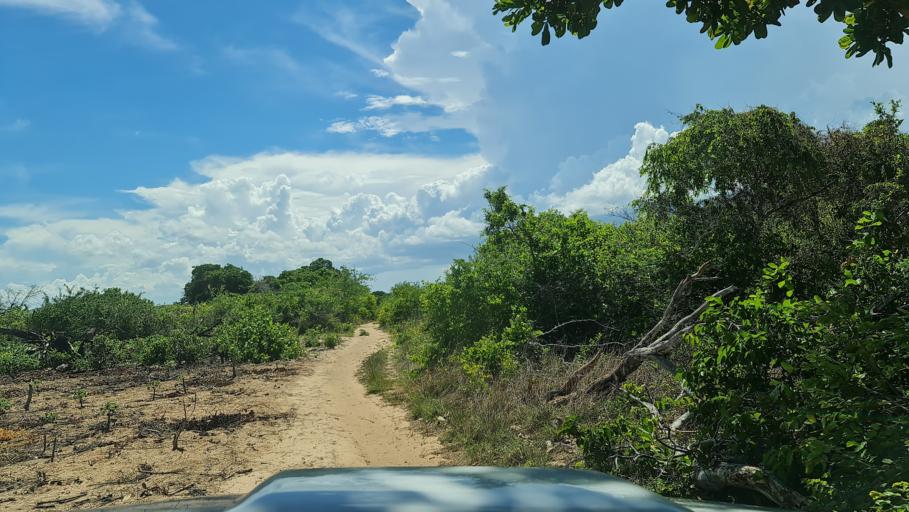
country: MZ
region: Nampula
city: Antonio Enes
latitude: -15.7074
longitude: 40.2549
